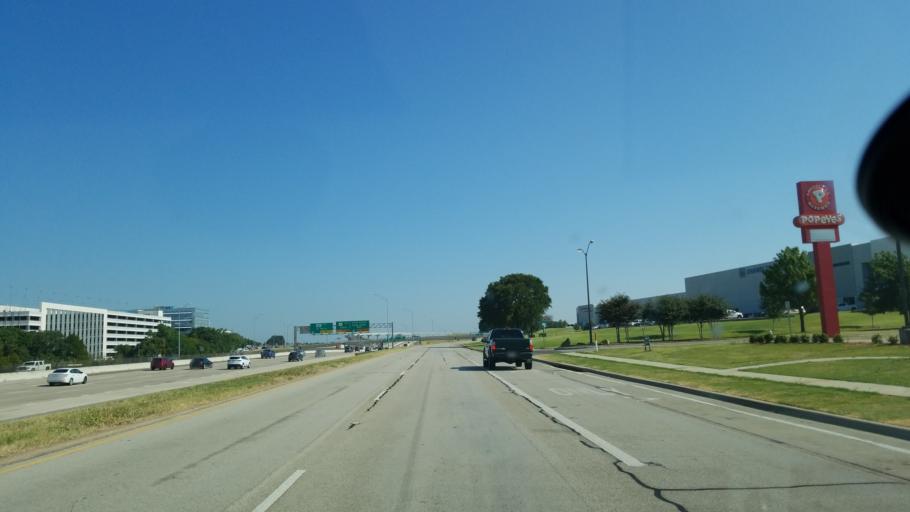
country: US
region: Texas
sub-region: Tarrant County
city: Euless
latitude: 32.8276
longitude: -97.0605
